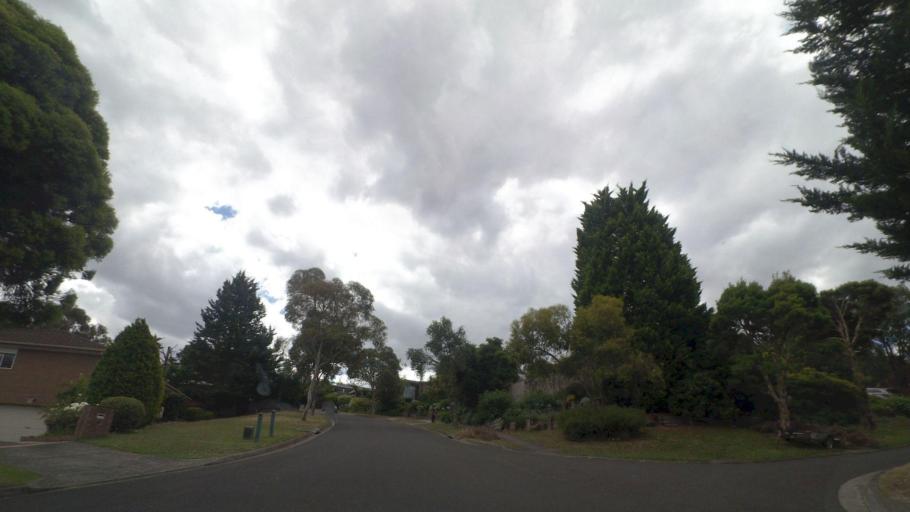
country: AU
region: Victoria
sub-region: Maroondah
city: Warranwood
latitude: -37.7716
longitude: 145.2545
